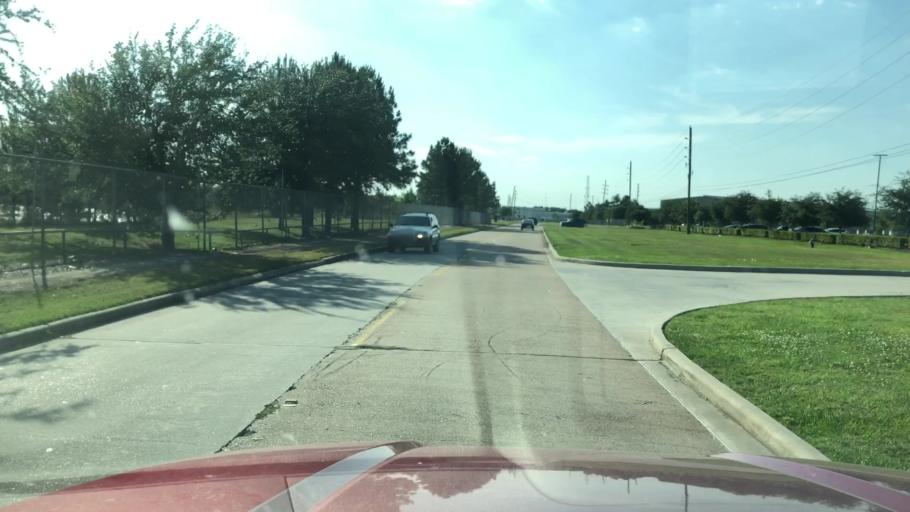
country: US
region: Texas
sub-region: Harris County
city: Hudson
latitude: 29.9433
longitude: -95.4911
